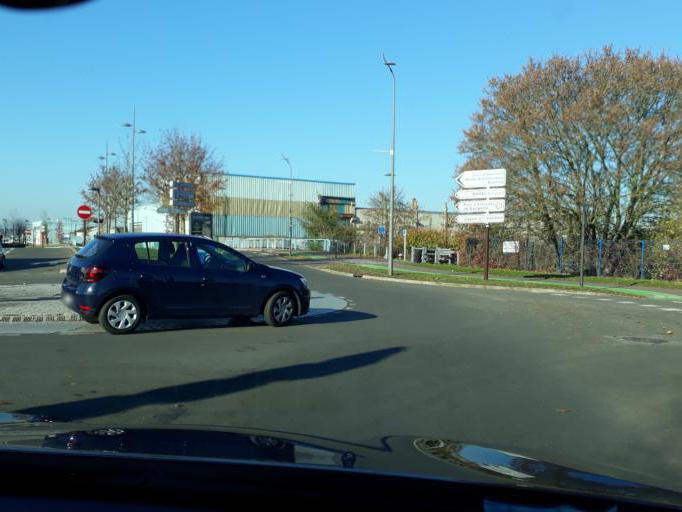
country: FR
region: Nord-Pas-de-Calais
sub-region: Departement du Nord
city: Douai
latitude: 50.3801
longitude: 3.0890
